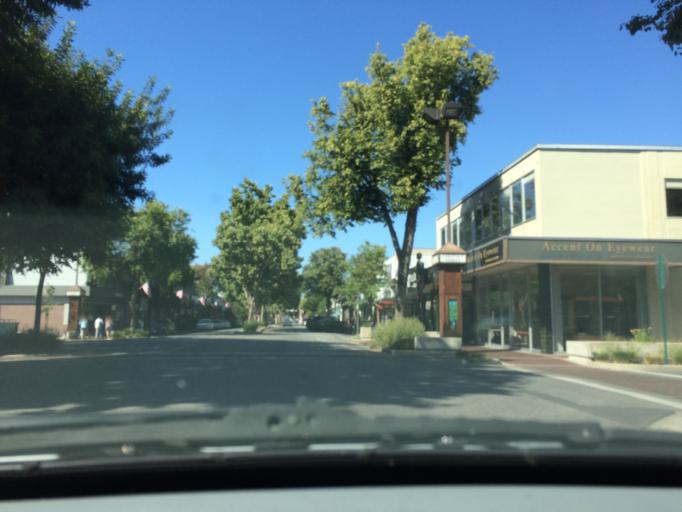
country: US
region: California
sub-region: San Mateo County
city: Menlo Park
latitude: 37.4514
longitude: -122.1847
